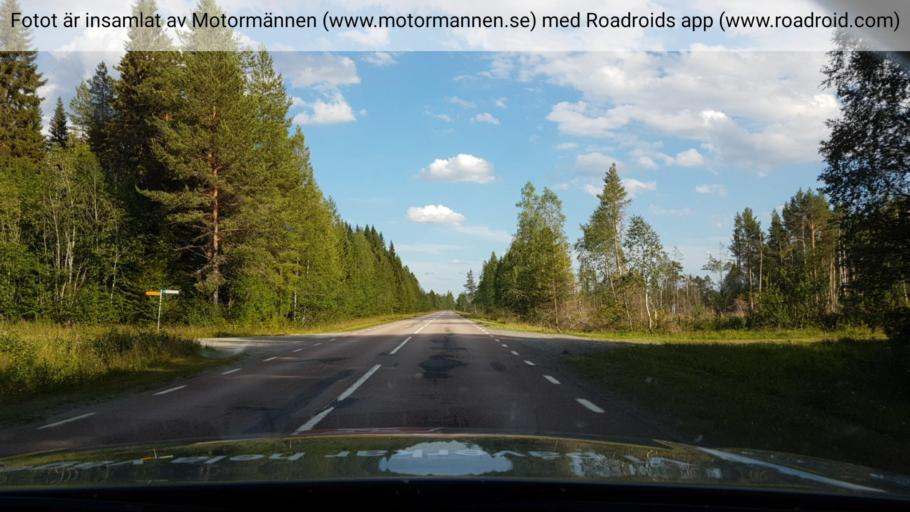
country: SE
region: Jaemtland
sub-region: Stroemsunds Kommun
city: Stroemsund
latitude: 63.6821
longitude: 15.9192
